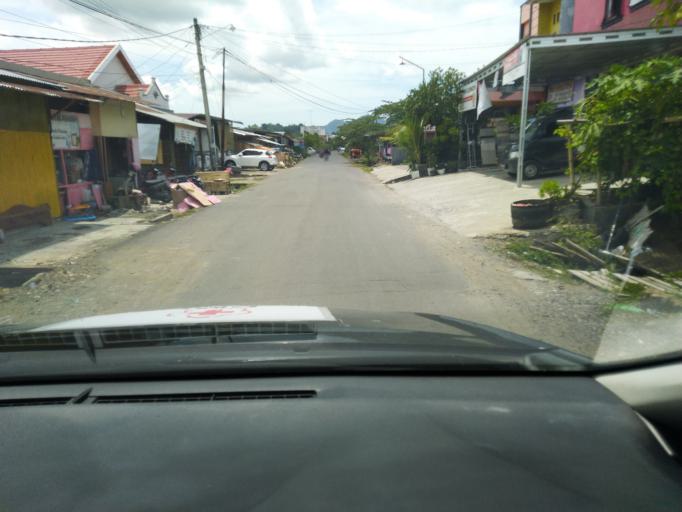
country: ID
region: Sulawesi Barat
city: Mamuju
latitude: -2.6811
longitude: 118.8810
